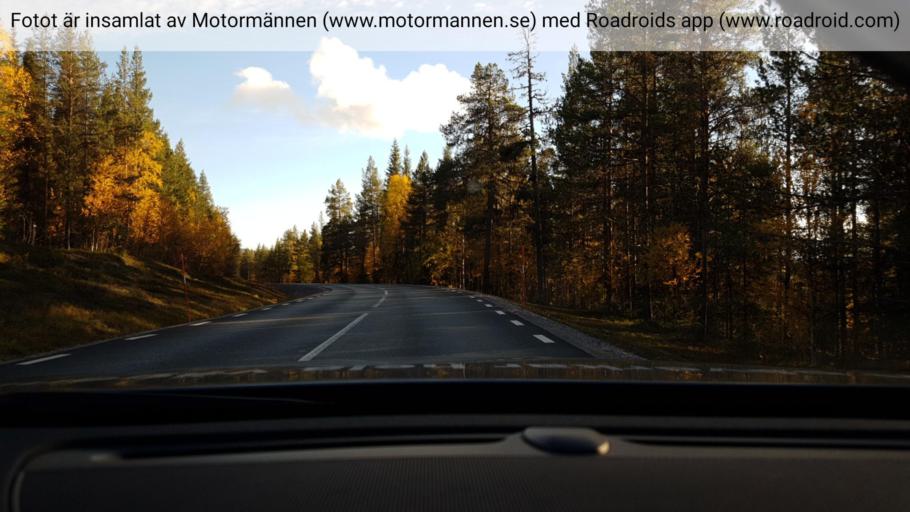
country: SE
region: Norrbotten
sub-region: Jokkmokks Kommun
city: Jokkmokk
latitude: 66.9266
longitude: 19.8249
